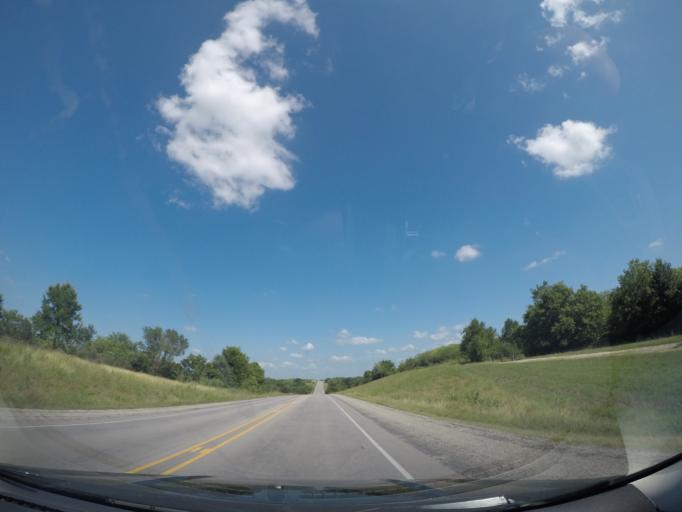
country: US
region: Texas
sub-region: Guadalupe County
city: Seguin
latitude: 29.5662
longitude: -97.8093
